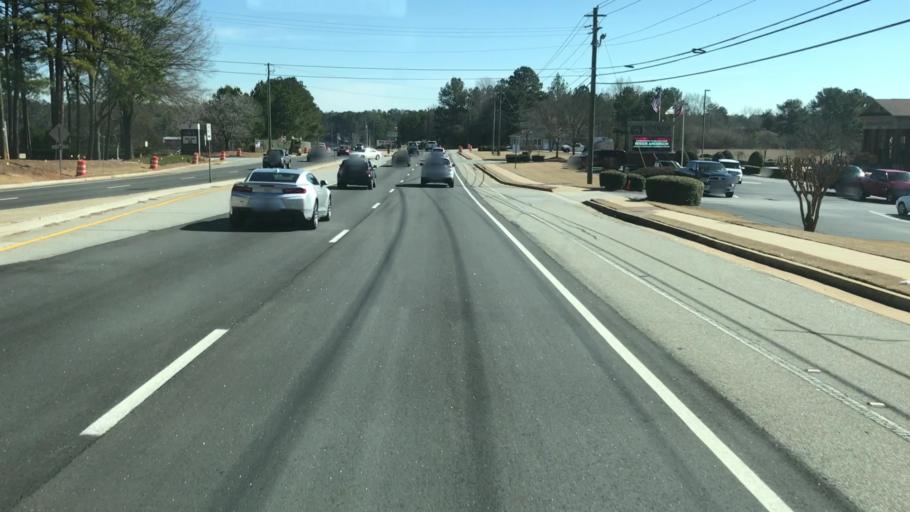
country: US
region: Georgia
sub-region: Gwinnett County
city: Lawrenceville
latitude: 33.9190
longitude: -84.0044
